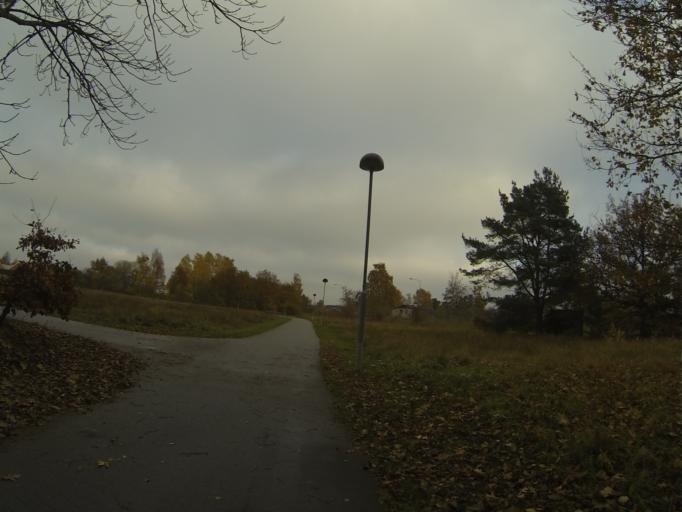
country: SE
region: Skane
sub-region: Lunds Kommun
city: Genarp
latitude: 55.7198
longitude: 13.3547
